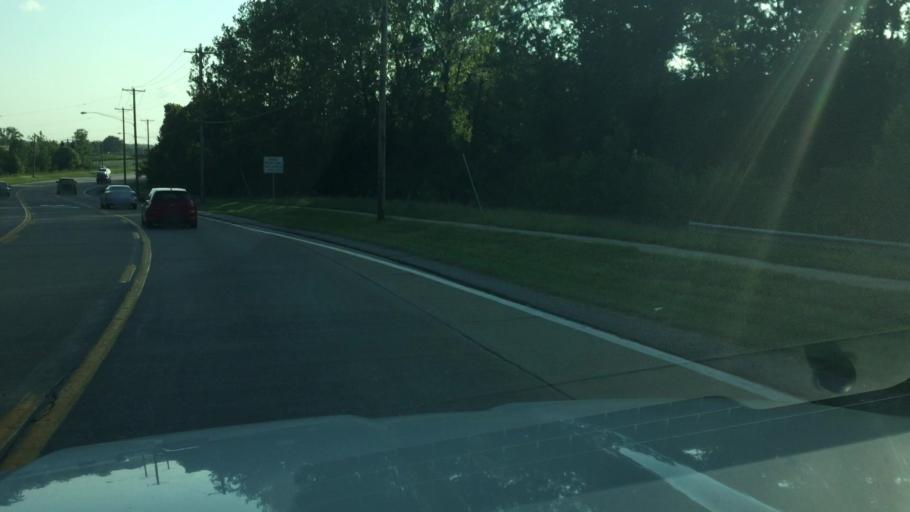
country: US
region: Missouri
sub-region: Jefferson County
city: Arnold
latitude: 38.4647
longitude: -90.3608
